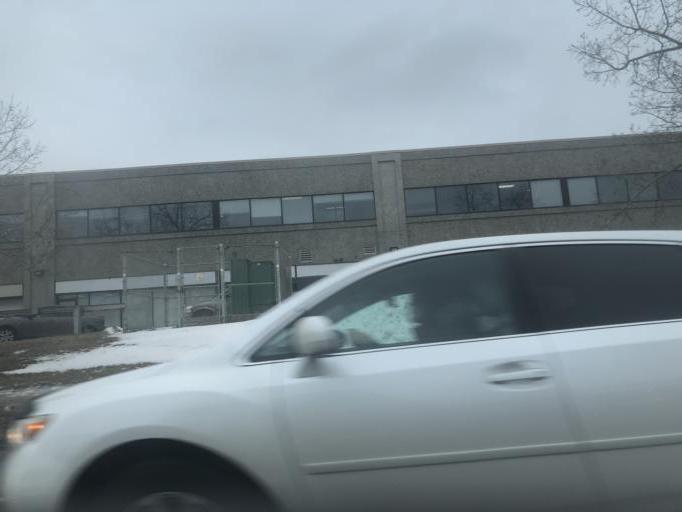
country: CA
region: Alberta
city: Calgary
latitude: 51.1011
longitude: -114.0365
